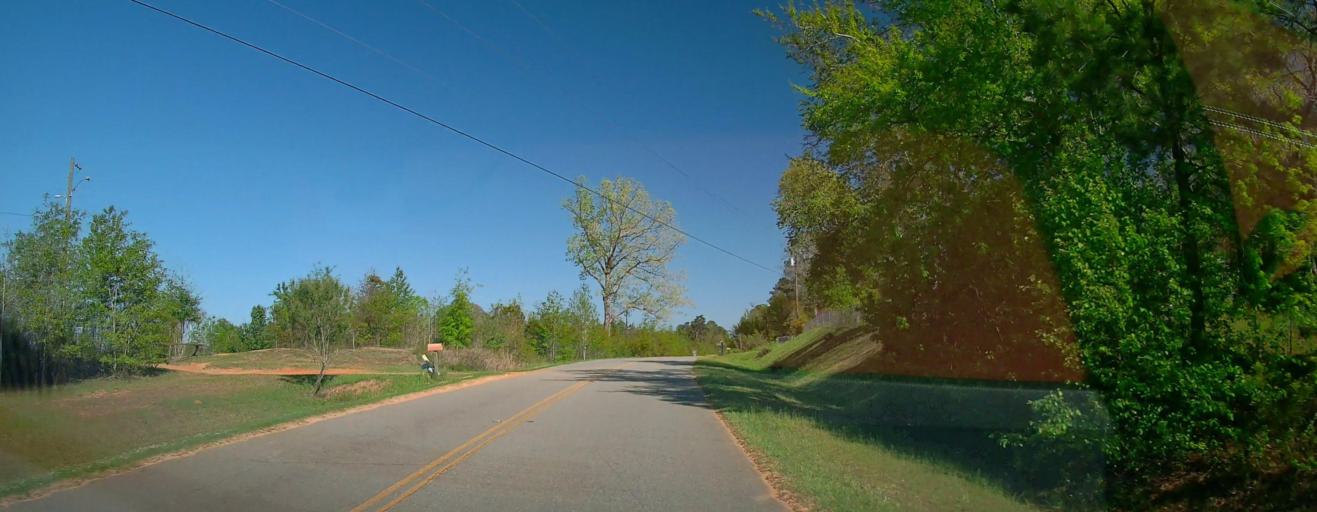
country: US
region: Georgia
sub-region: Pulaski County
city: Hawkinsville
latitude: 32.2401
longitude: -83.5117
